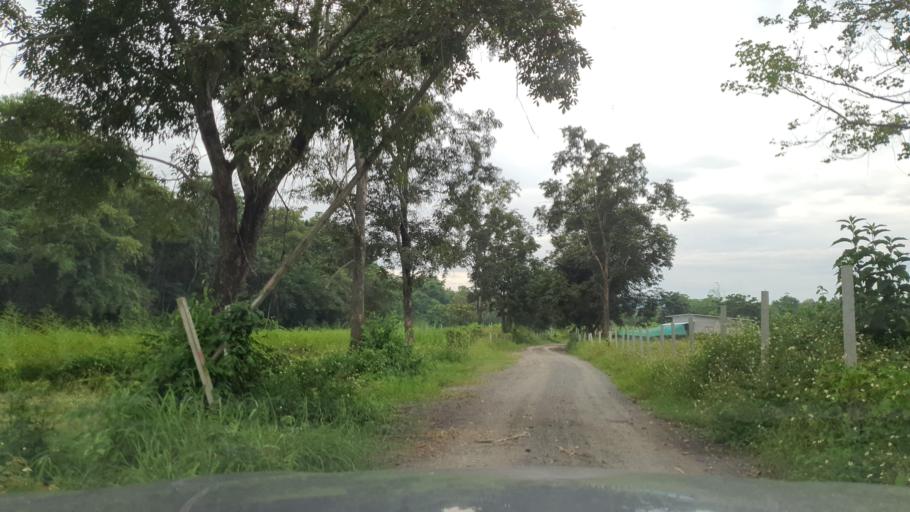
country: TH
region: Chiang Mai
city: San Sai
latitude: 18.9425
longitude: 98.9095
